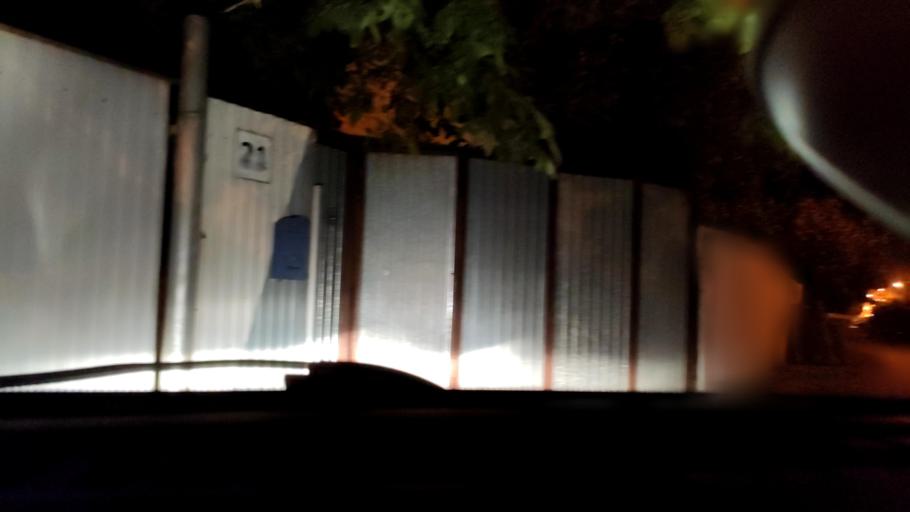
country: RU
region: Samara
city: Samara
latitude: 53.1780
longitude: 50.1791
